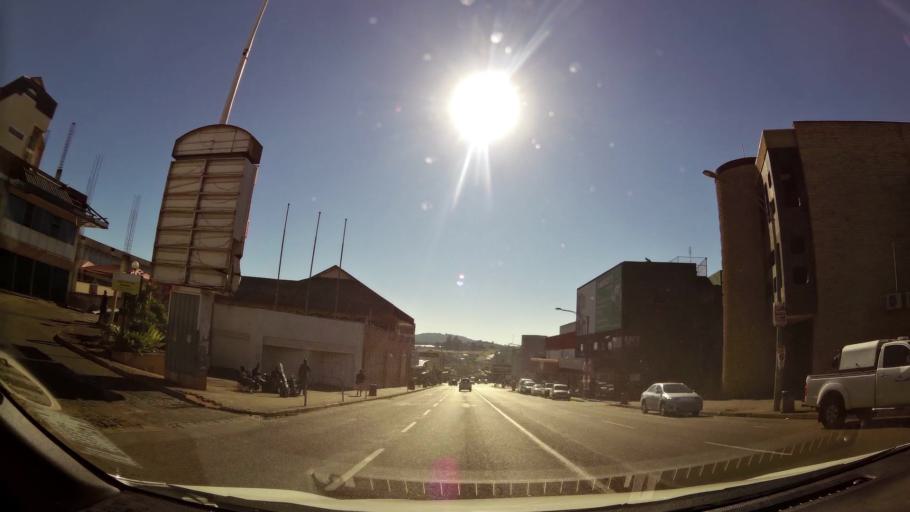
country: ZA
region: Limpopo
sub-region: Mopani District Municipality
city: Tzaneen
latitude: -23.8266
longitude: 30.1598
